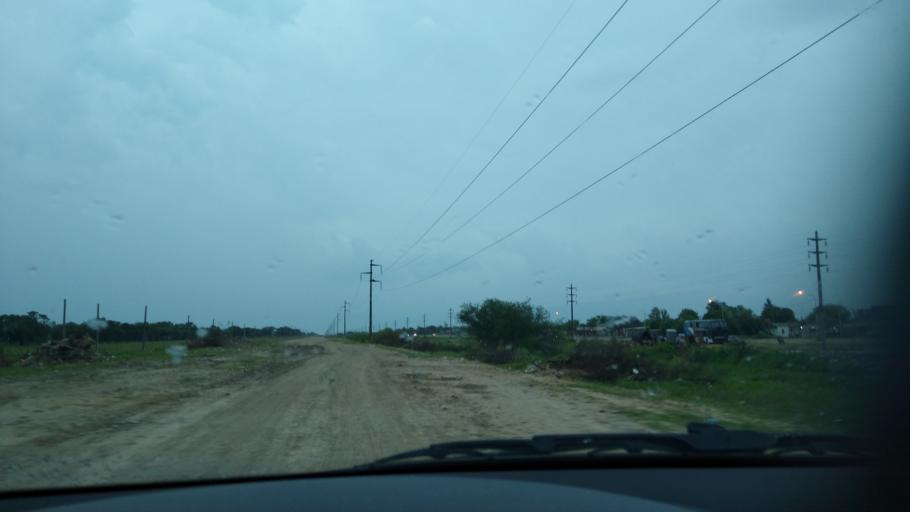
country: AR
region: Chaco
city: Puerto Vilelas
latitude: -27.5032
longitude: -58.9721
